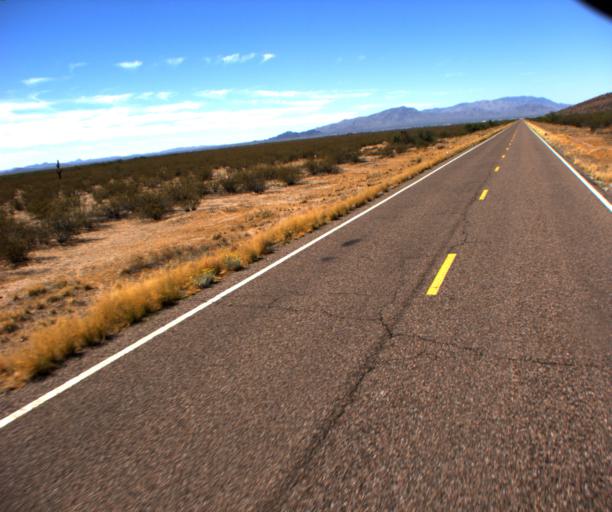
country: US
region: Arizona
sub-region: Yavapai County
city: Congress
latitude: 34.0212
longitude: -113.0952
